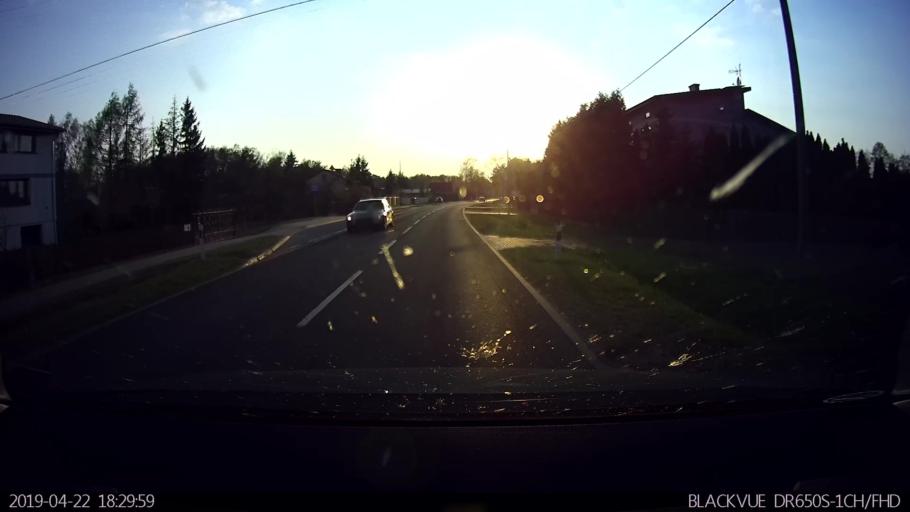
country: PL
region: Masovian Voivodeship
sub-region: Powiat wolominski
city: Tluszcz
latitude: 52.4519
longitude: 21.4424
